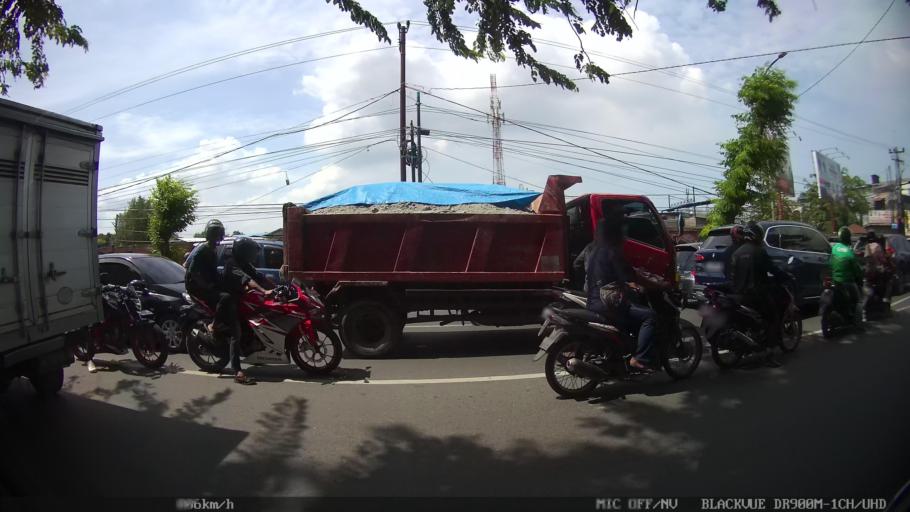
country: ID
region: North Sumatra
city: Medan
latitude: 3.6072
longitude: 98.6736
